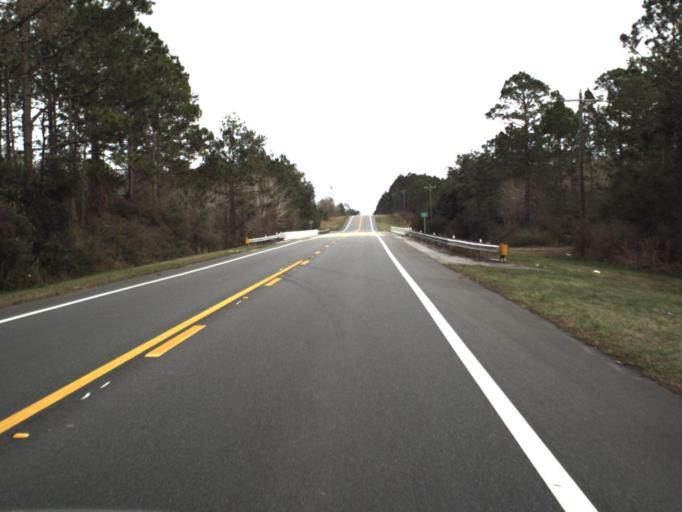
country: US
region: Florida
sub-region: Bay County
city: Callaway
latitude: 30.1411
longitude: -85.4086
